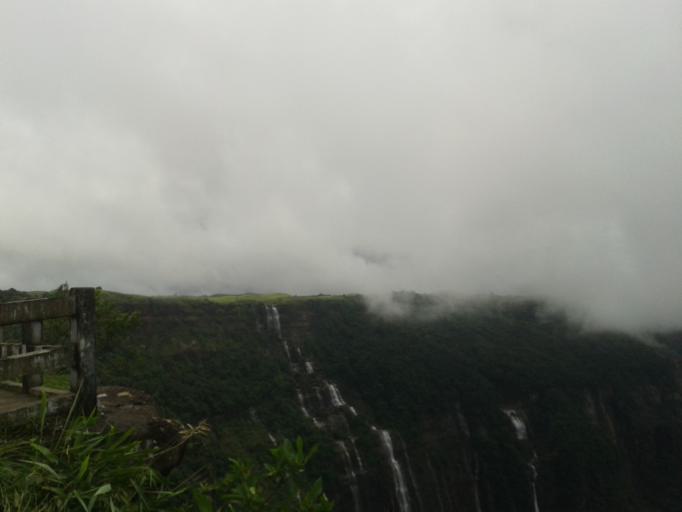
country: IN
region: Meghalaya
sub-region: East Khasi Hills
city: Cherrapunji
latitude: 25.2383
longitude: 91.7327
